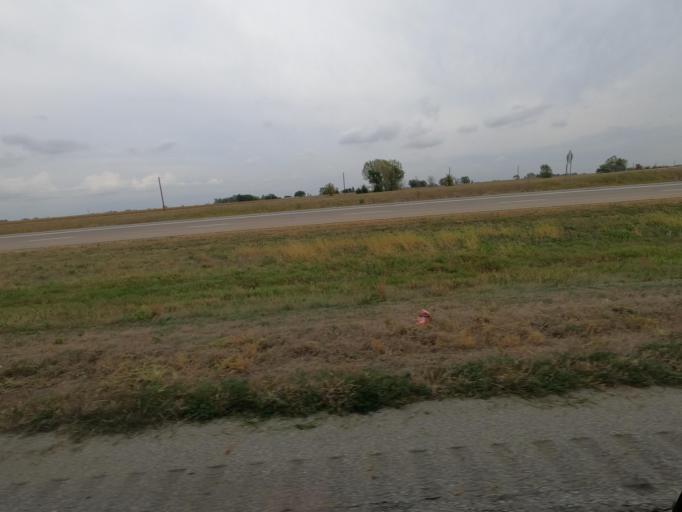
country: US
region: Iowa
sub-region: Jasper County
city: Monroe
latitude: 41.5459
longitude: -93.1306
